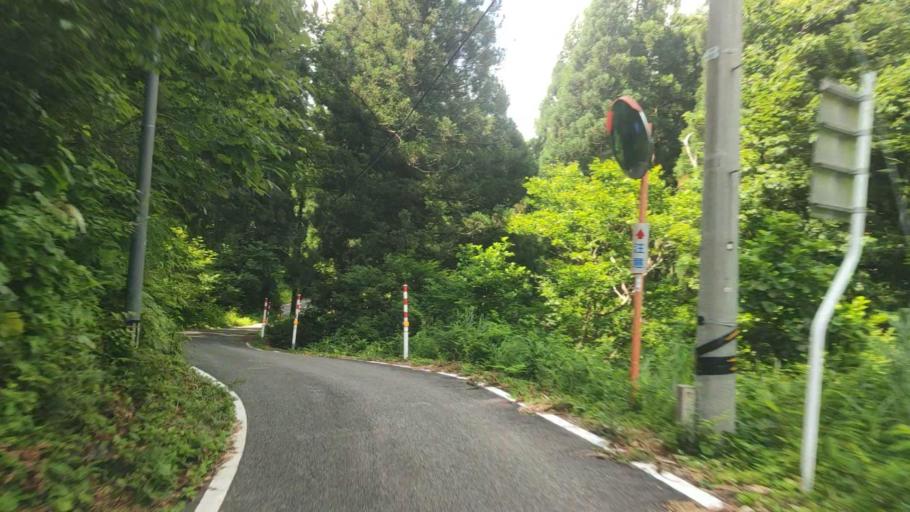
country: JP
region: Fukui
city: Katsuyama
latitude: 36.2116
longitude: 136.5282
